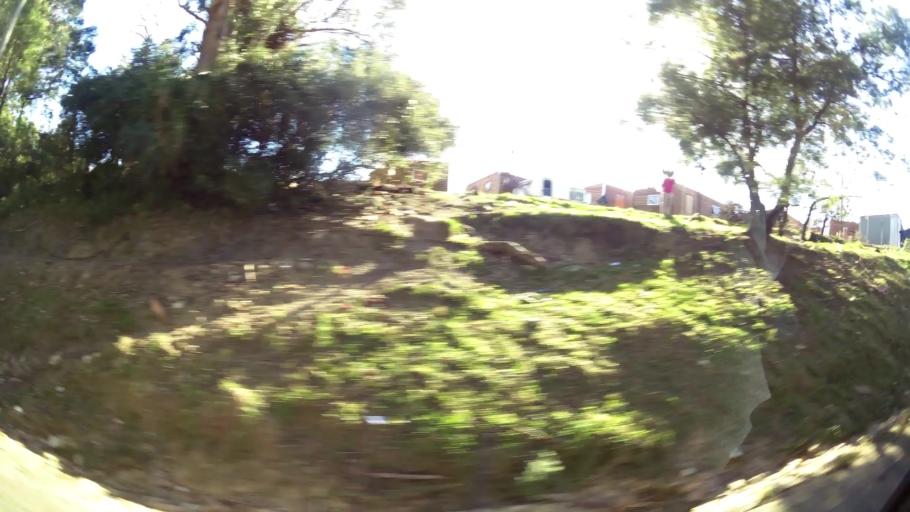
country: ZA
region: Western Cape
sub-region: Eden District Municipality
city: Knysna
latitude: -34.0271
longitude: 23.0543
